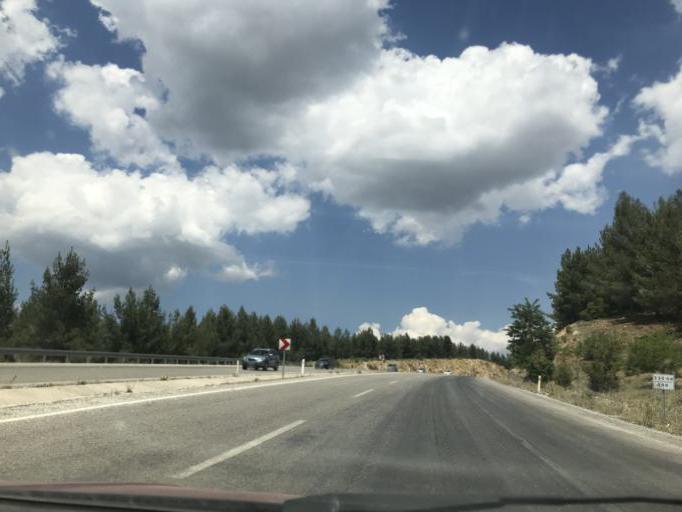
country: TR
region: Denizli
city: Tavas
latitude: 37.5802
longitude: 29.0910
